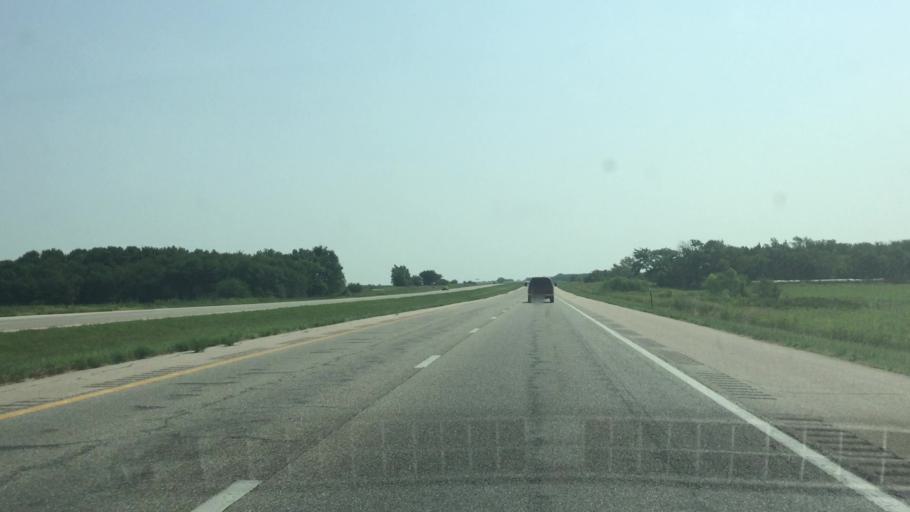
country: US
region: Kansas
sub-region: Osage County
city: Lyndon
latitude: 38.4266
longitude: -95.7688
